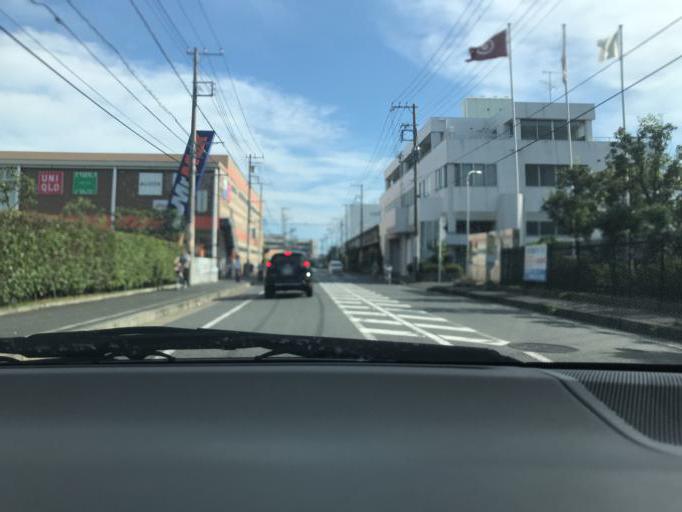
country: JP
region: Kanagawa
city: Fujisawa
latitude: 35.3404
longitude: 139.4629
